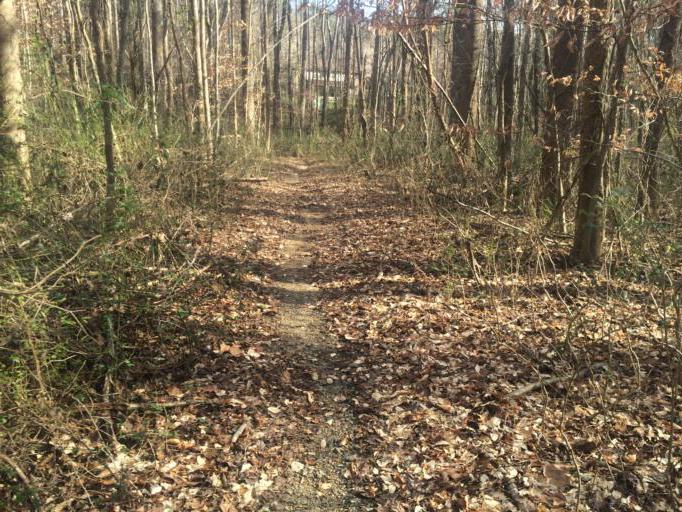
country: US
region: North Carolina
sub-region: Polk County
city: Columbus
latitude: 35.2384
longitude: -82.2173
